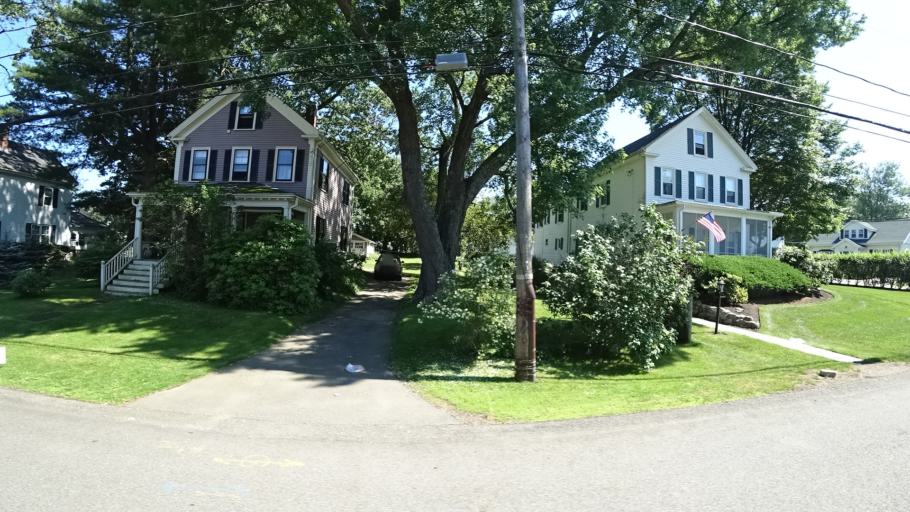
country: US
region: Massachusetts
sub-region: Norfolk County
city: Dedham
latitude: 42.2388
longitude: -71.1526
